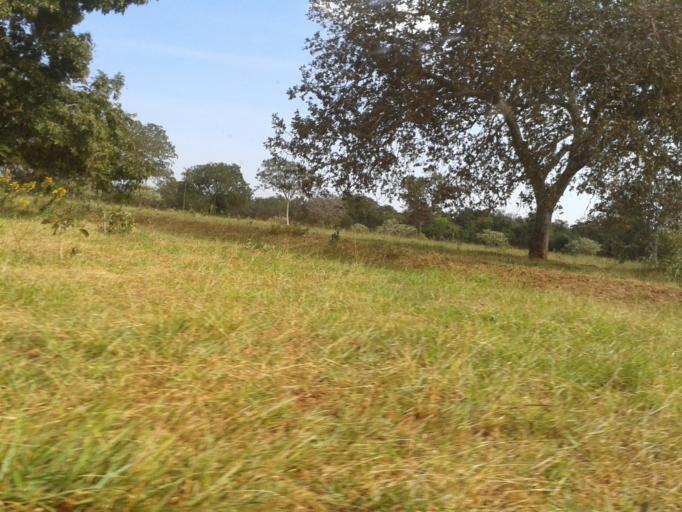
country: BR
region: Minas Gerais
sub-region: Ituiutaba
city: Ituiutaba
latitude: -19.0614
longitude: -49.3642
